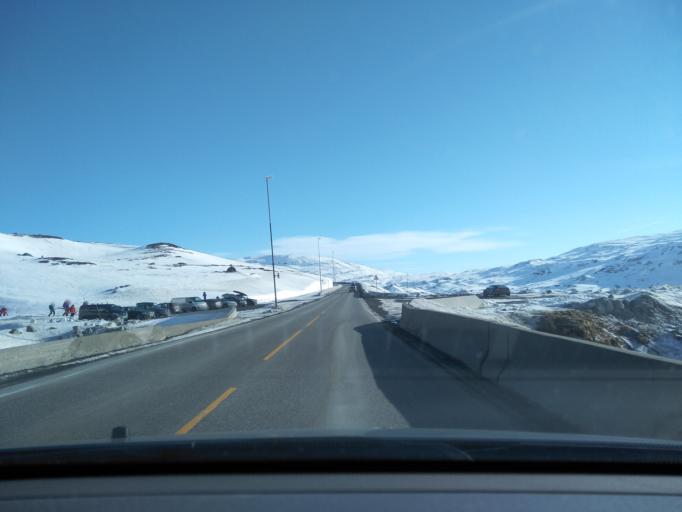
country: NO
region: Aust-Agder
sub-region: Bykle
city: Hovden
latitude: 59.8448
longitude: 6.9725
